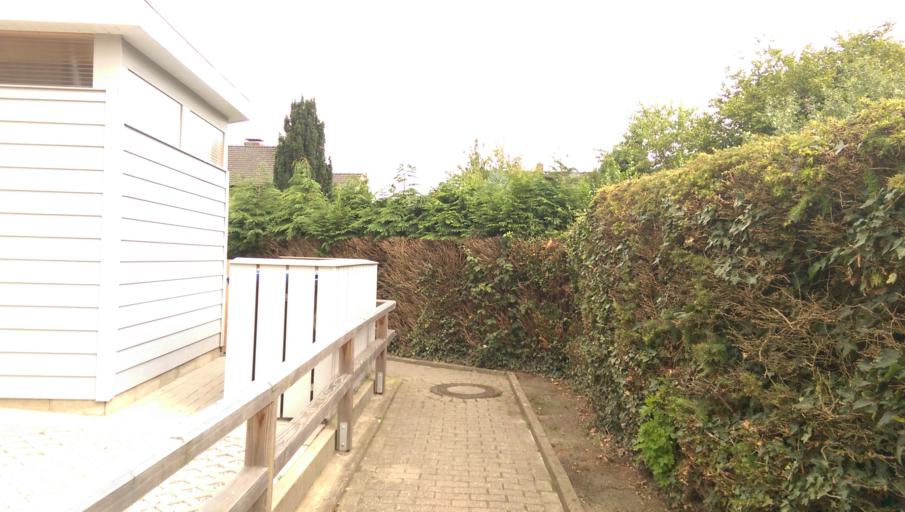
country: DE
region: Lower Saxony
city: Bockhorn
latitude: 53.3941
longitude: 8.0158
